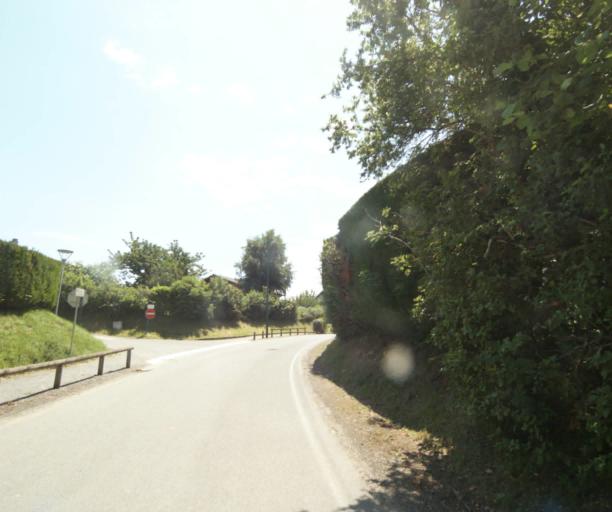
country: FR
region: Rhone-Alpes
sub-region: Departement de la Haute-Savoie
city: Messery
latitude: 46.3650
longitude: 6.3257
